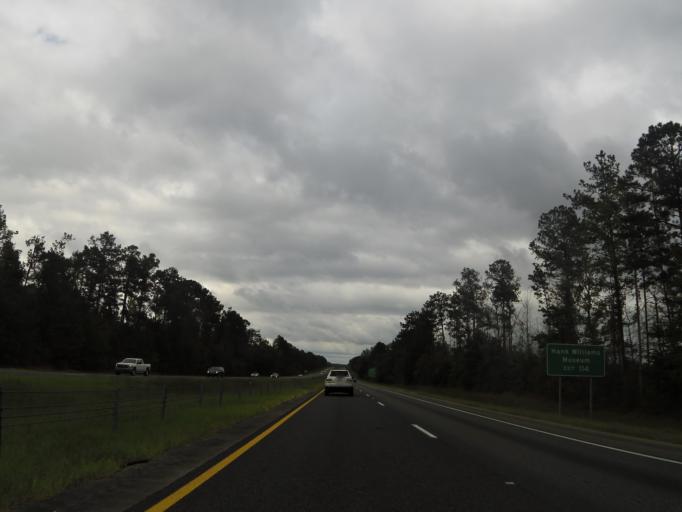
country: US
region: Alabama
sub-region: Butler County
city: Georgiana
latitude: 31.6378
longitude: -86.7884
